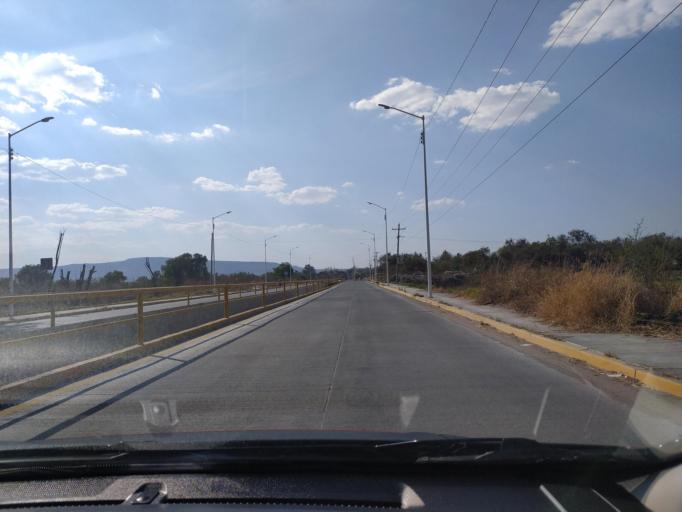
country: MX
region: Guanajuato
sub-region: San Francisco del Rincon
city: Fraccionamiento la Mezquitera
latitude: 21.0159
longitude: -101.8282
